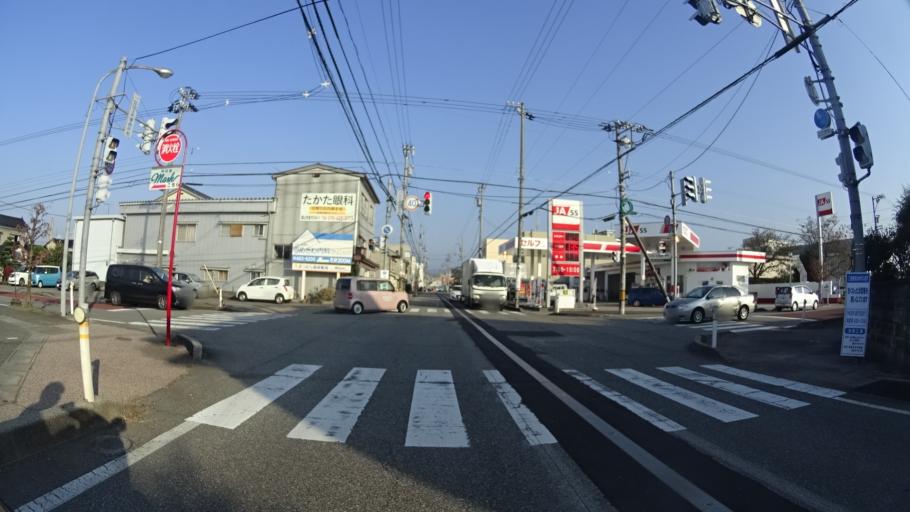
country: JP
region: Toyama
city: Kamiichi
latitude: 36.6641
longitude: 137.3121
